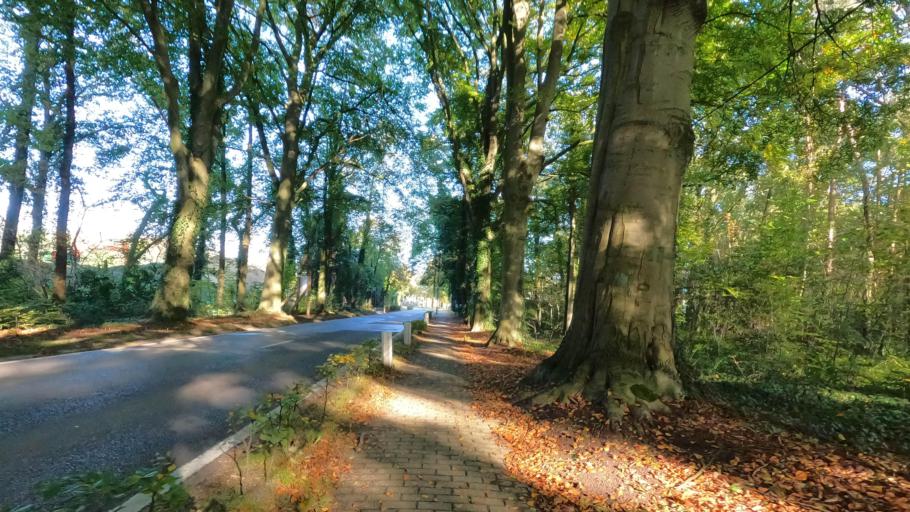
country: BE
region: Flanders
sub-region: Provincie Antwerpen
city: Schilde
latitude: 51.2846
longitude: 4.5706
